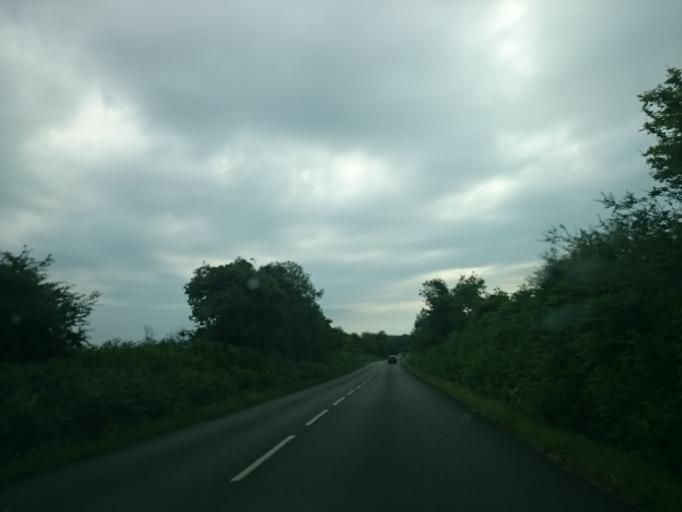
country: FR
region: Brittany
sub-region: Departement du Finistere
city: Ploumoguer
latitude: 48.3840
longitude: -4.7050
